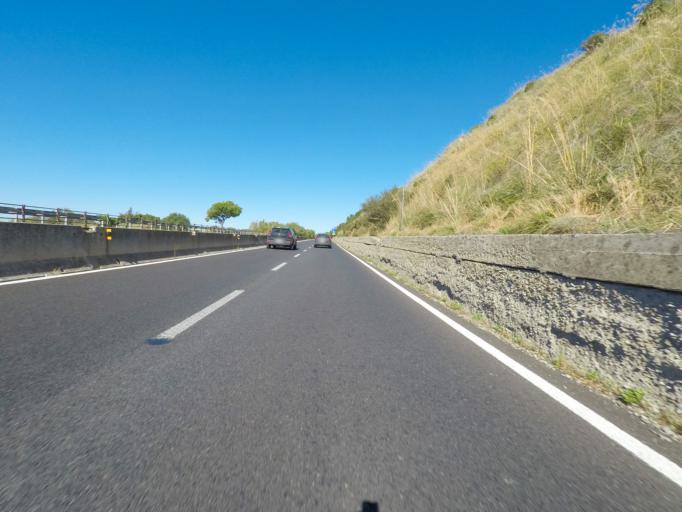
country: IT
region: Tuscany
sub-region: Provincia di Grosseto
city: Fonteblanda
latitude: 42.5586
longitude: 11.1716
